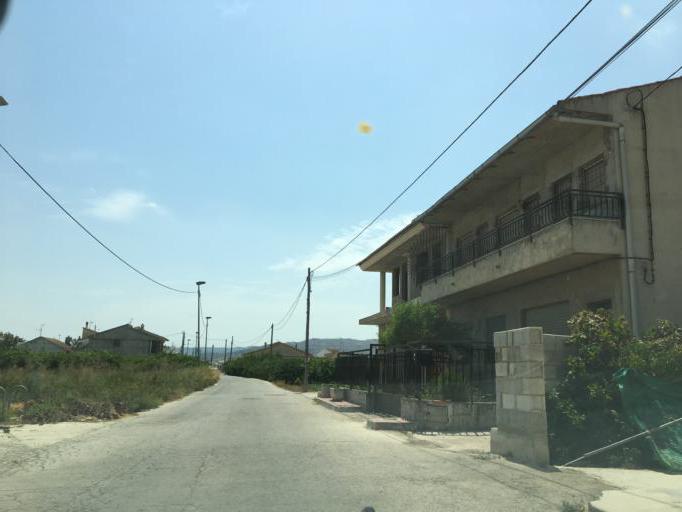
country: ES
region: Murcia
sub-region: Murcia
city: Santomera
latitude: 38.0246
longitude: -1.0472
